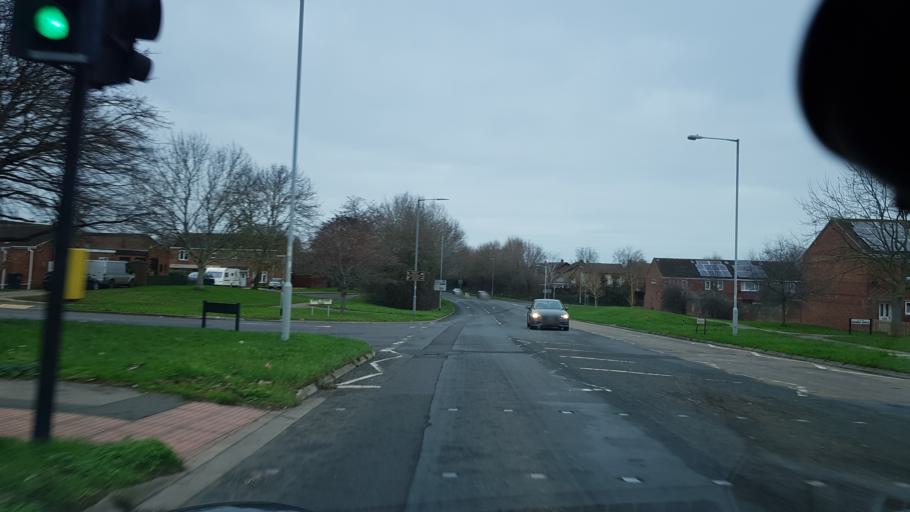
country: GB
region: England
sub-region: Somerset
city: Taunton
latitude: 51.0062
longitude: -3.0775
